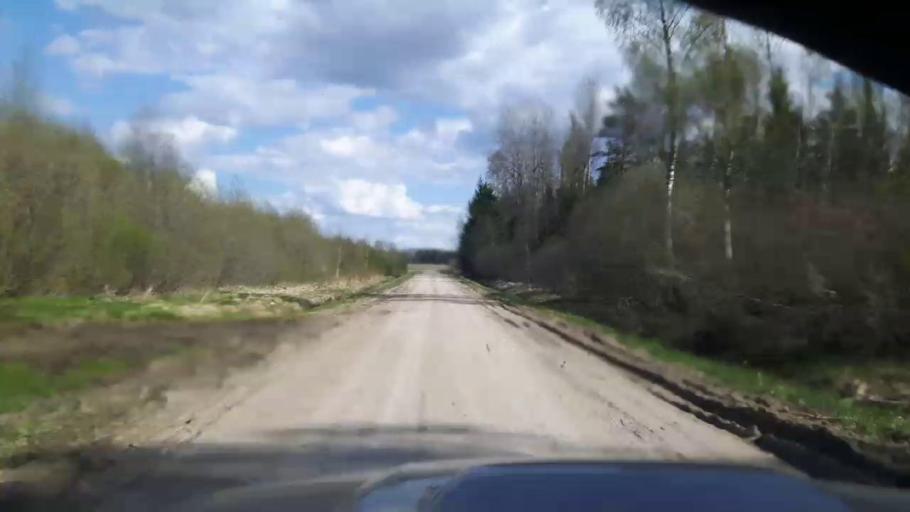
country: EE
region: Paernumaa
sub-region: Tootsi vald
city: Tootsi
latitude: 58.4459
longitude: 24.8455
